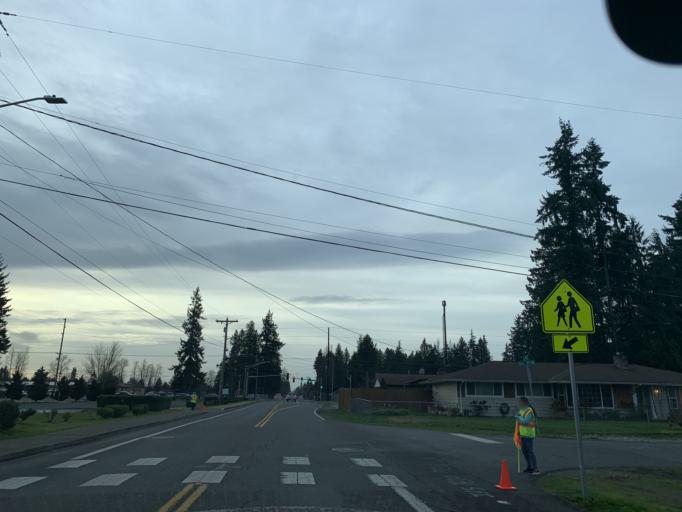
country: US
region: Washington
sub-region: Snohomish County
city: Marysville
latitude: 48.0871
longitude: -122.1622
